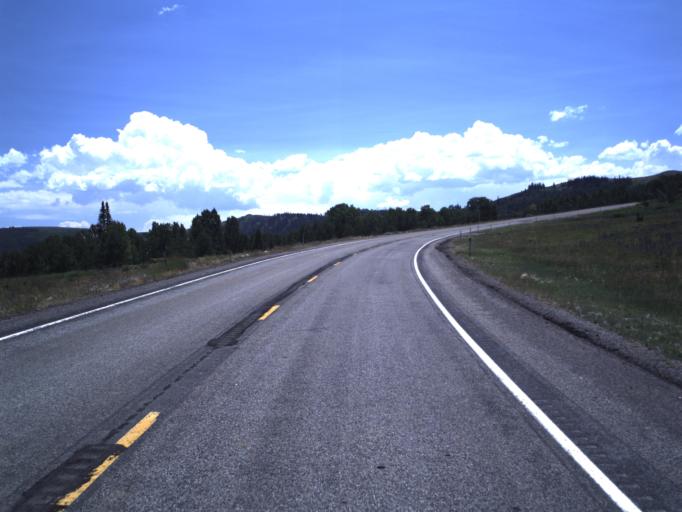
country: US
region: Utah
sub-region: Sanpete County
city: Fairview
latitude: 39.6514
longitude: -111.3290
